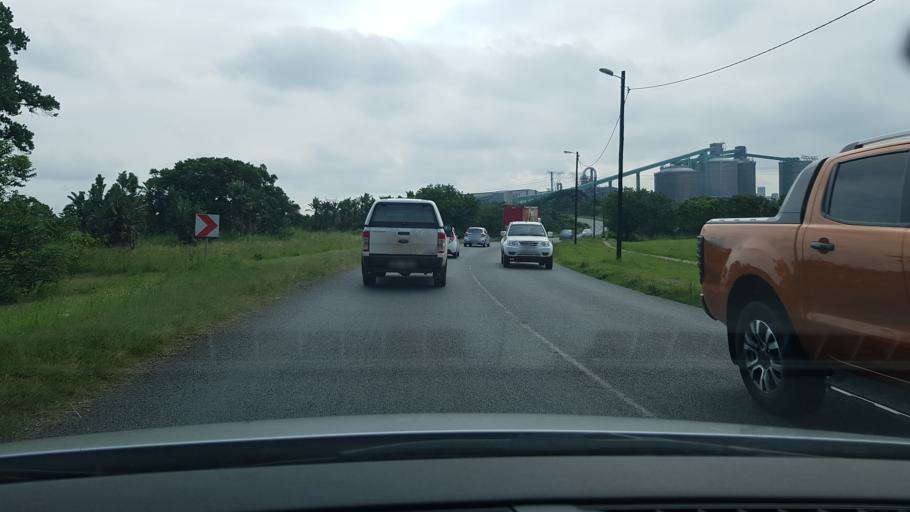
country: ZA
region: KwaZulu-Natal
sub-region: uThungulu District Municipality
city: Richards Bay
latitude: -28.7623
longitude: 32.0423
